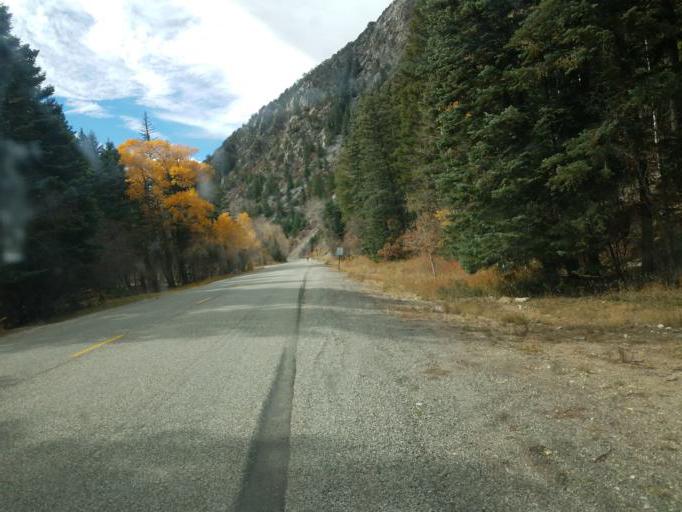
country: US
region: New Mexico
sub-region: Taos County
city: Arroyo Seco
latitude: 36.5493
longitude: -105.5480
